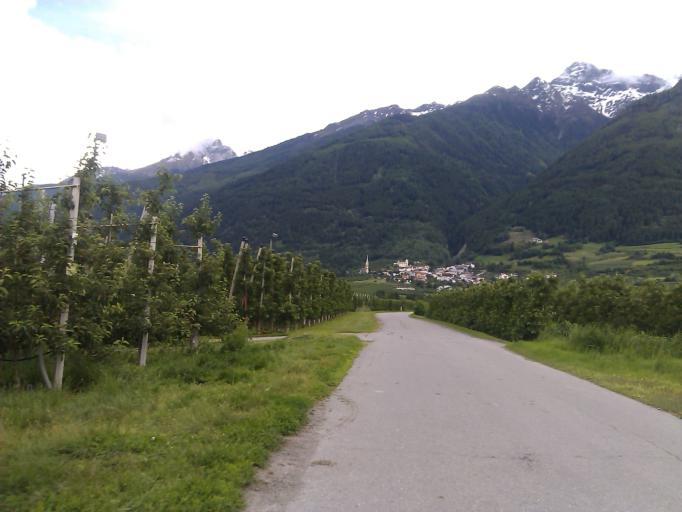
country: IT
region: Trentino-Alto Adige
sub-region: Bolzano
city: Prato Allo Stelvio
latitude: 46.6238
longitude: 10.6243
